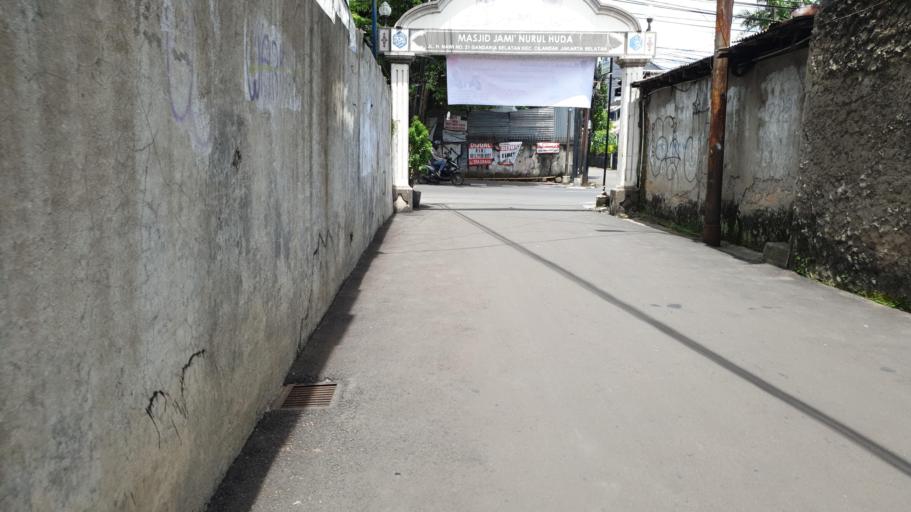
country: ID
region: Jakarta Raya
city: Jakarta
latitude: -6.2641
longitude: 106.7898
